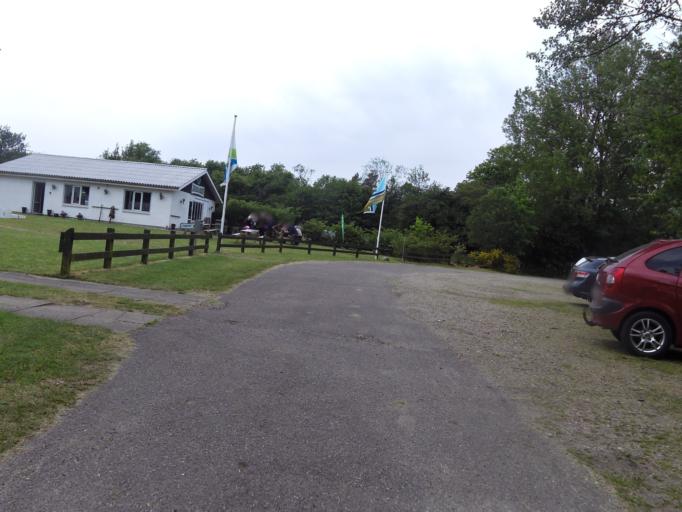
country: DK
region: South Denmark
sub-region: Esbjerg Kommune
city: Ribe
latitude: 55.3229
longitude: 8.8228
